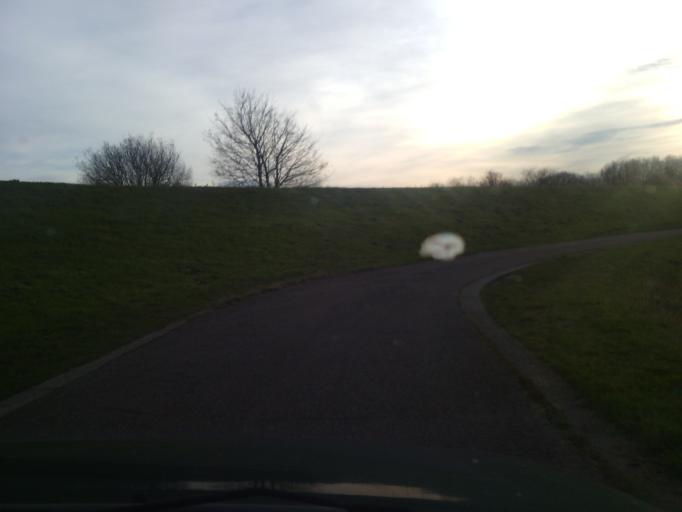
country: BE
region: Flanders
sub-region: Provincie Oost-Vlaanderen
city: Berlare
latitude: 51.0221
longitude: 4.0409
